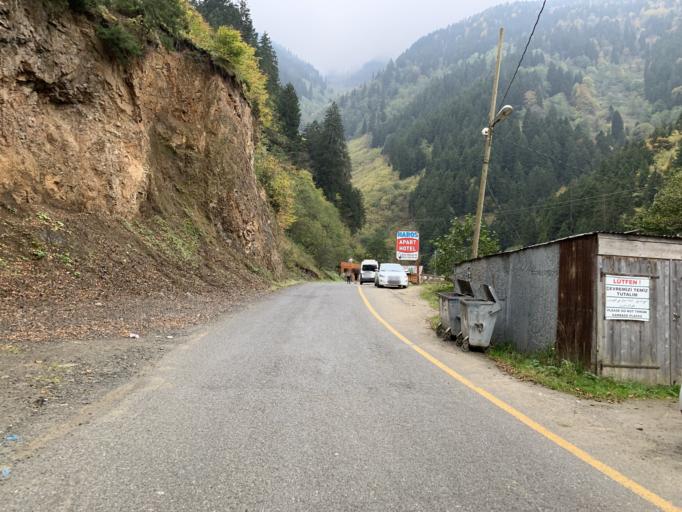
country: TR
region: Trabzon
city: Uzungol
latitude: 40.5964
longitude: 40.3215
